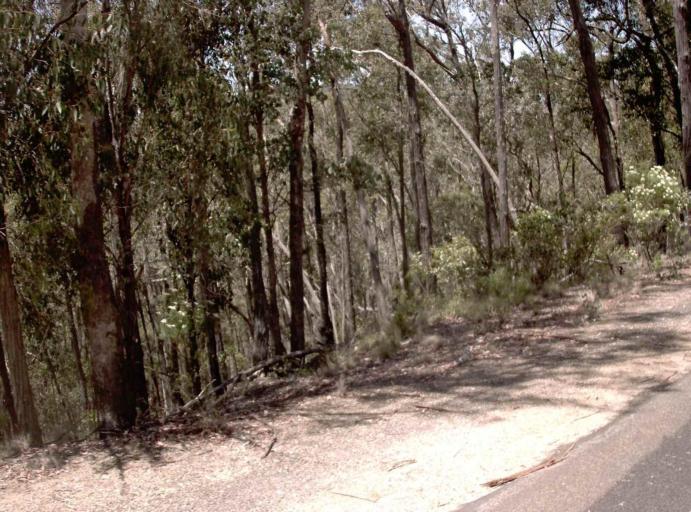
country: AU
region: Victoria
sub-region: East Gippsland
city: Lakes Entrance
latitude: -37.6129
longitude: 147.8817
